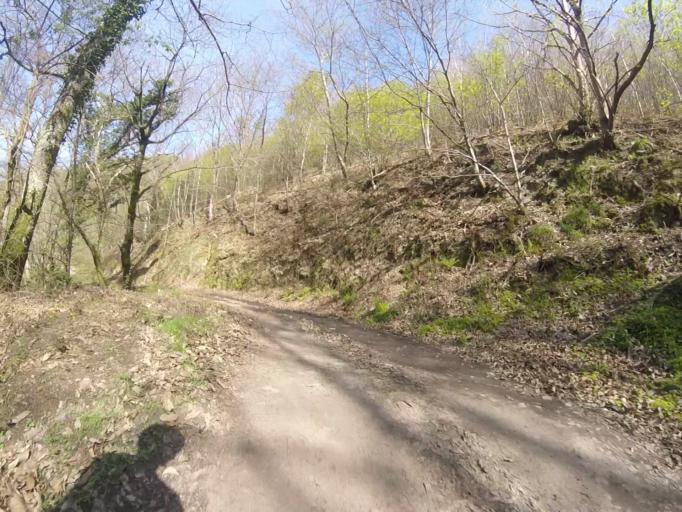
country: ES
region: Basque Country
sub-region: Provincia de Guipuzcoa
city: Irun
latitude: 43.2658
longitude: -1.8058
